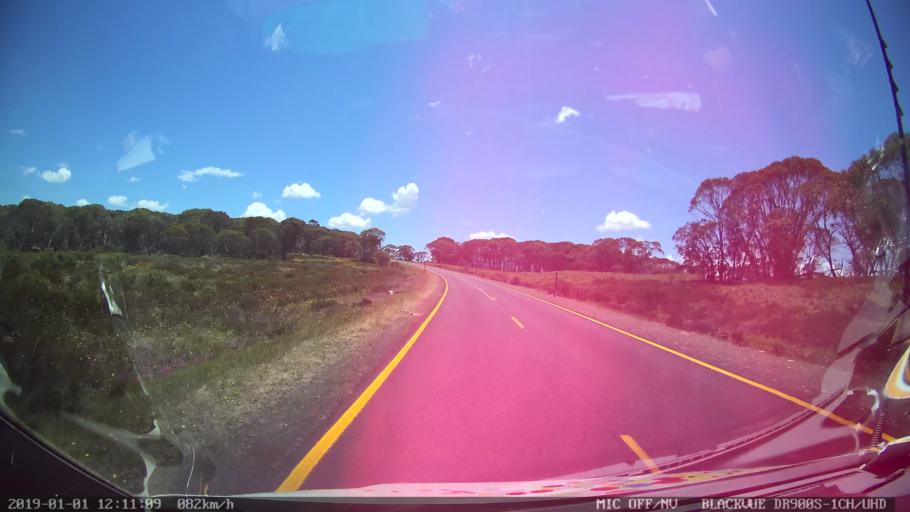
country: AU
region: New South Wales
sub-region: Tumut Shire
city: Tumut
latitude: -35.7872
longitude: 148.5062
